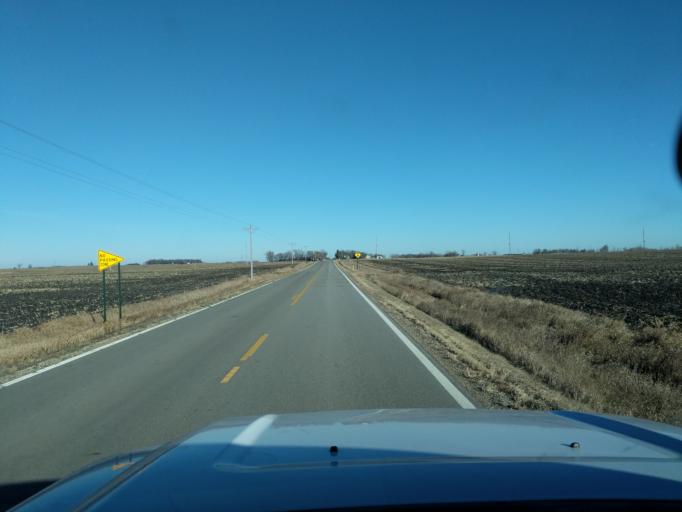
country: US
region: Minnesota
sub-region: Yellow Medicine County
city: Granite Falls
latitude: 44.7857
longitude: -95.4017
